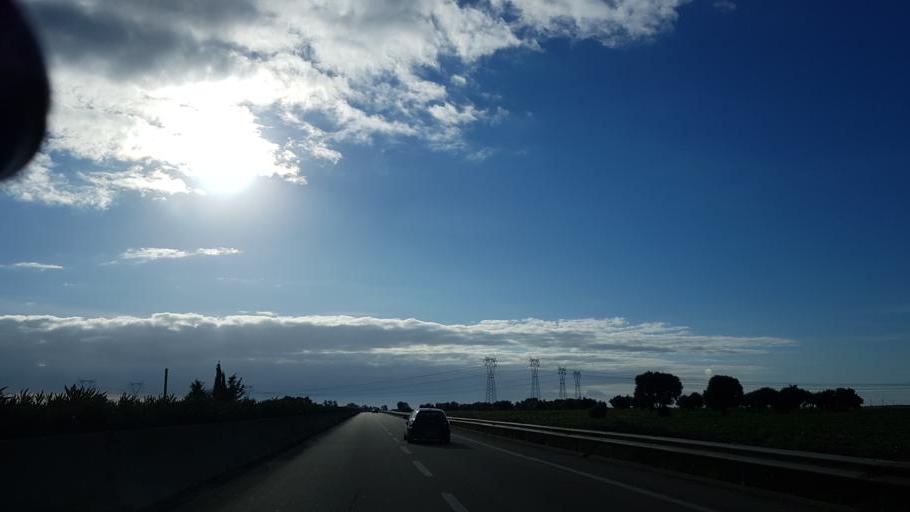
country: IT
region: Apulia
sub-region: Provincia di Brindisi
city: Tuturano
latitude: 40.5654
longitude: 17.9869
